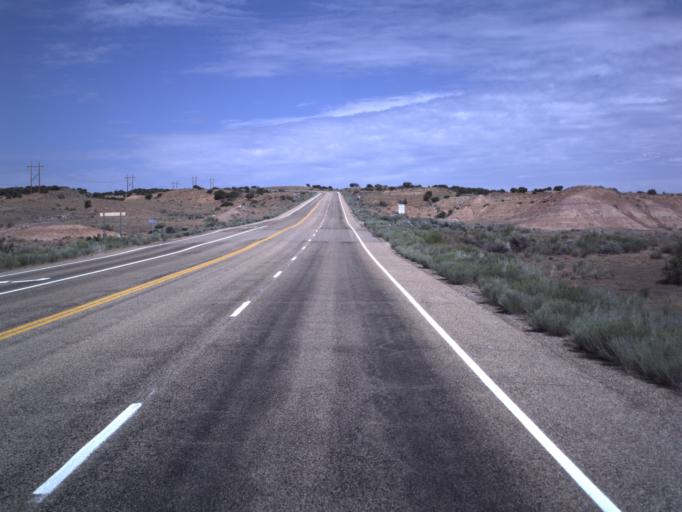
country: US
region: Utah
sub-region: Uintah County
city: Naples
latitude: 40.1358
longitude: -109.2683
